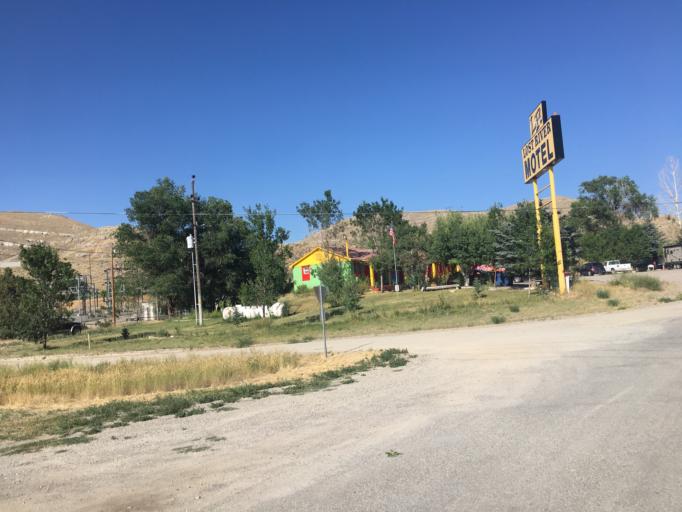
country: US
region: Idaho
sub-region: Butte County
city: Arco
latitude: 43.6340
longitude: -113.2962
